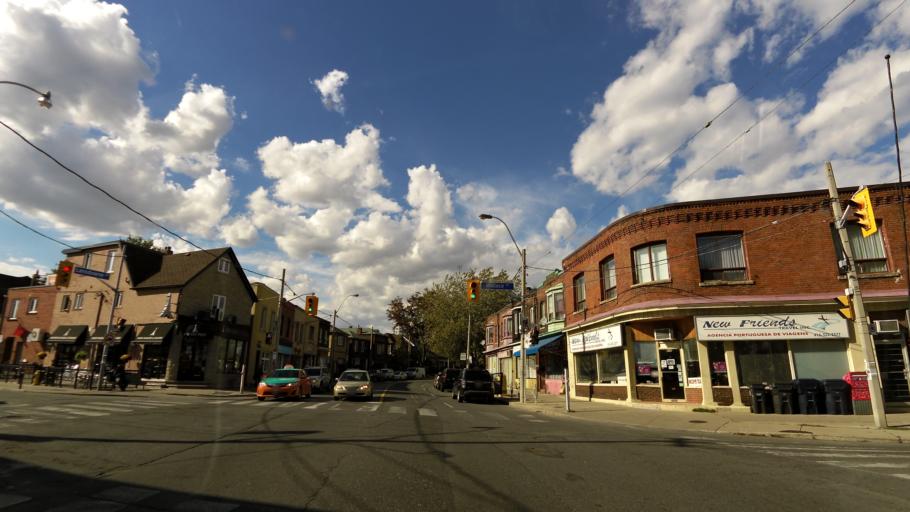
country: CA
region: Ontario
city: Toronto
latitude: 43.6622
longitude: -79.4443
